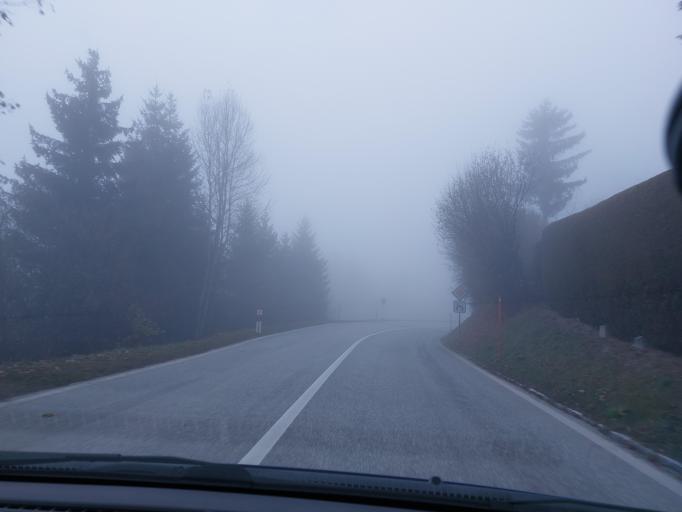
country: CH
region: Valais
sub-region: Sierre District
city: Randogne
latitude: 46.3112
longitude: 7.4948
